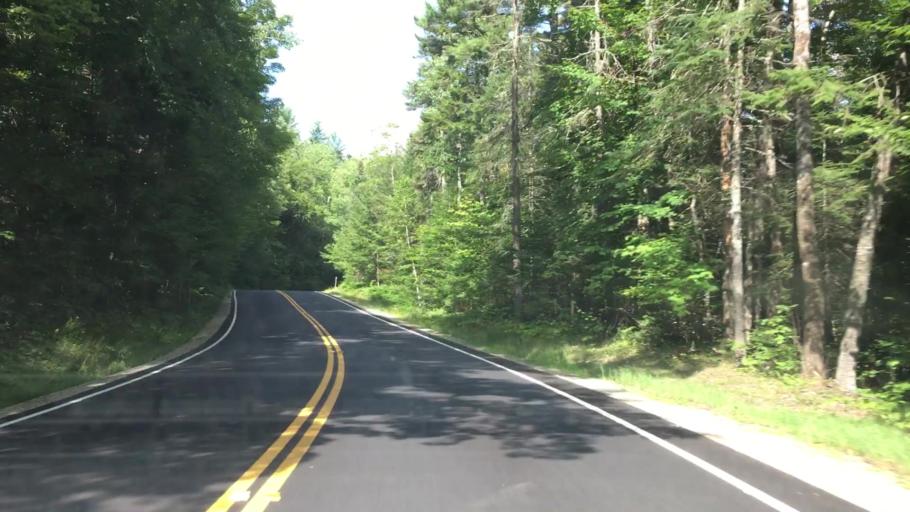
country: US
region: New Hampshire
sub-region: Grafton County
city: North Haverhill
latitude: 44.1006
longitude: -71.8593
